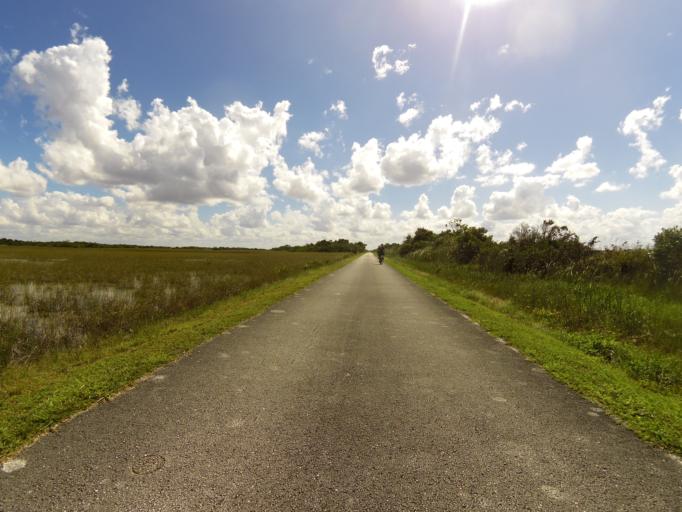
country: US
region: Florida
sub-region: Miami-Dade County
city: The Hammocks
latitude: 25.7115
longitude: -80.7667
